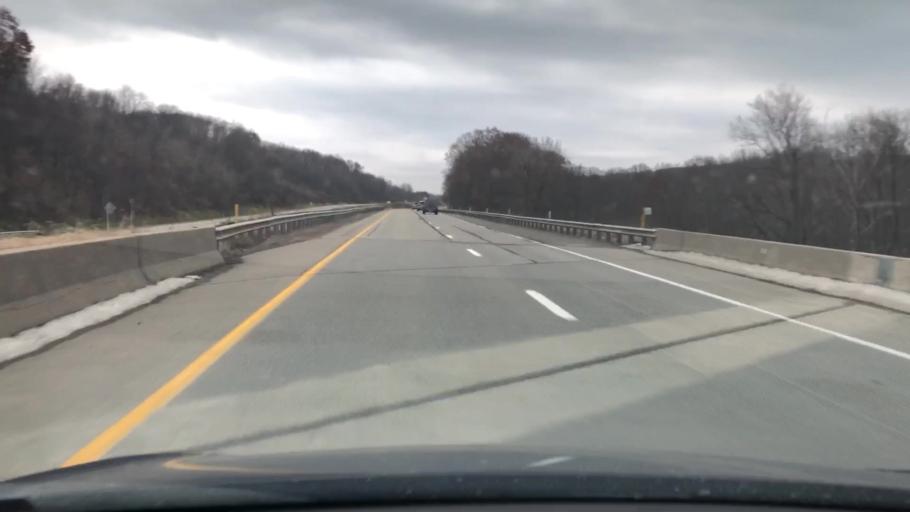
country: US
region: Pennsylvania
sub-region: Armstrong County
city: West Hills
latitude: 40.7972
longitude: -79.5715
